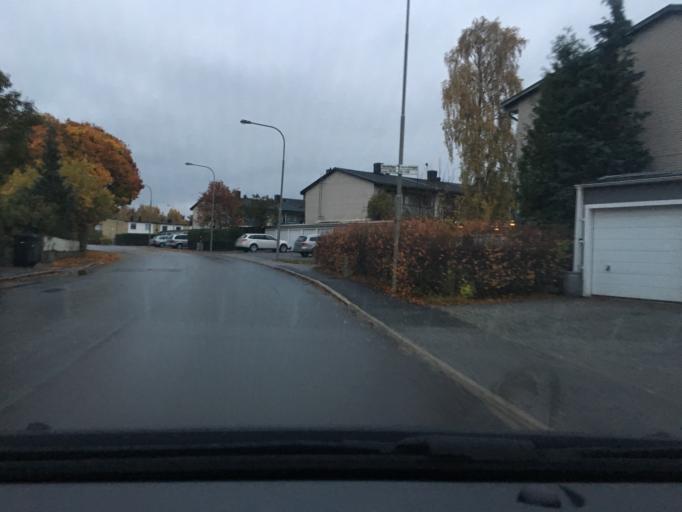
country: SE
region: Stockholm
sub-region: Stockholms Kommun
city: Bromma
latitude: 59.3741
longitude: 17.8890
